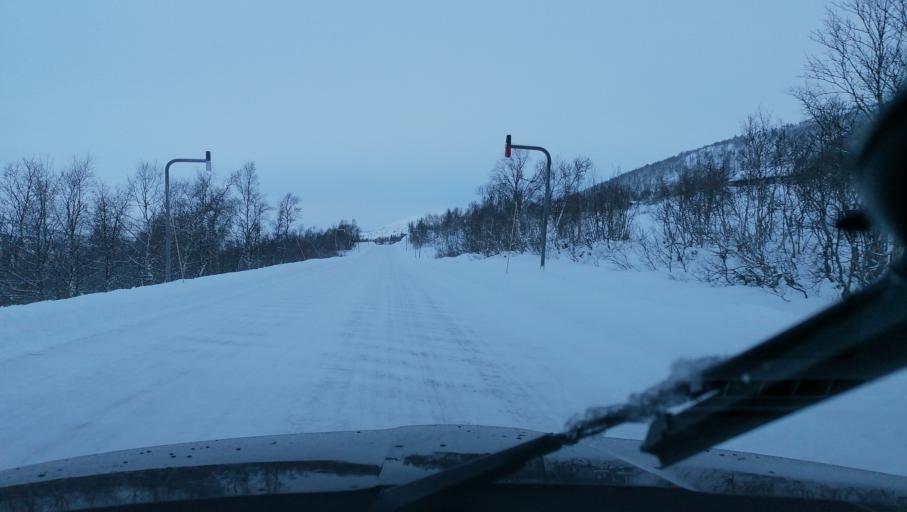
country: NO
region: Aust-Agder
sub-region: Bykle
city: Hovden
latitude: 59.6342
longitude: 7.4536
